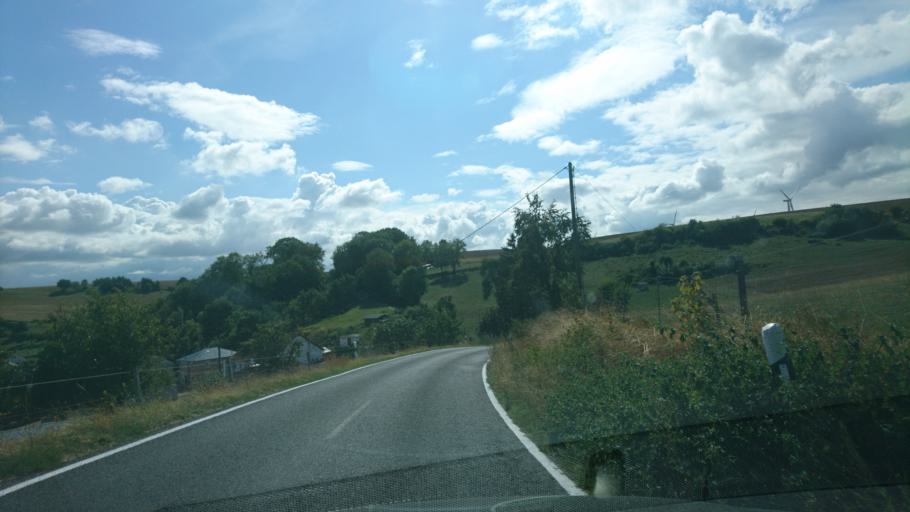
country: DE
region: Rheinland-Pfalz
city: Merzkirchen
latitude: 49.5731
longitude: 6.4894
